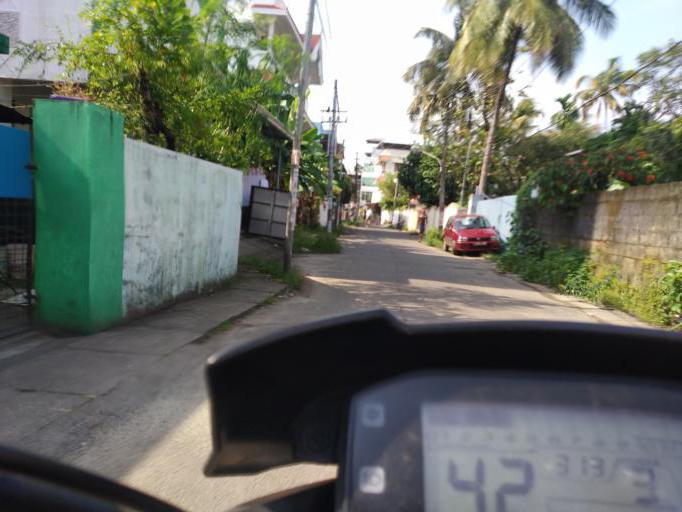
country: IN
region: Kerala
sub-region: Ernakulam
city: Cochin
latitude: 9.9818
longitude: 76.2935
